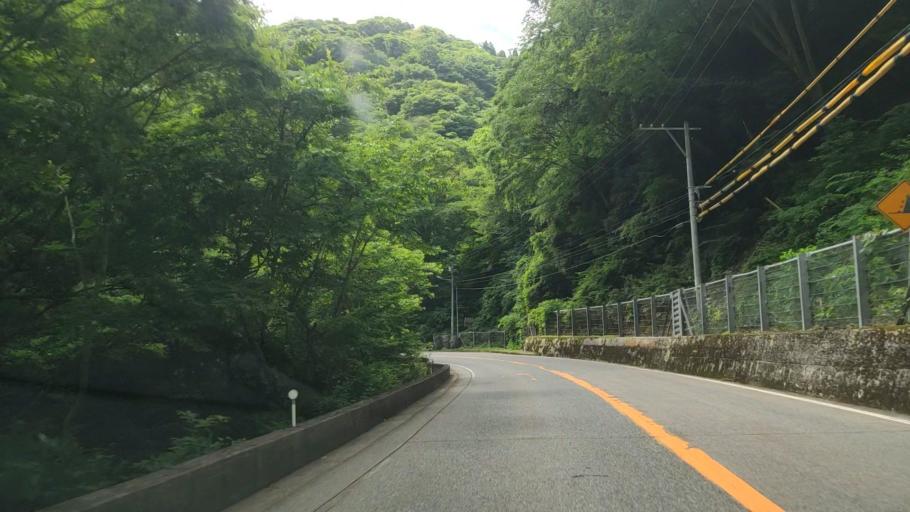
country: JP
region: Okayama
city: Niimi
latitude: 35.2127
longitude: 133.4840
